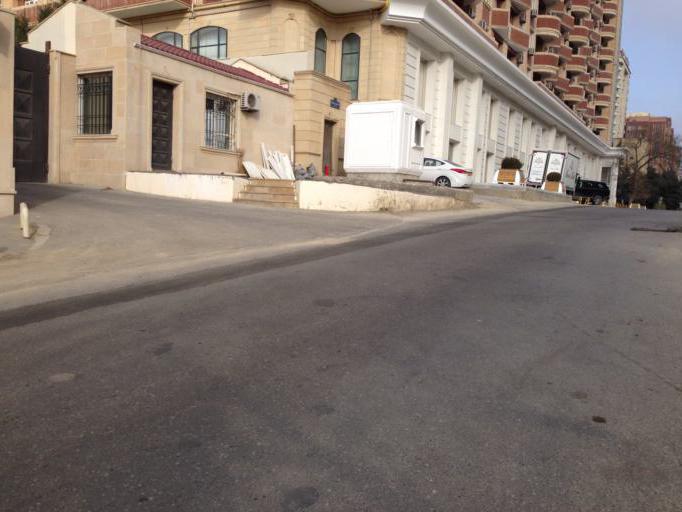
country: AZ
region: Baki
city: Baku
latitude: 40.3963
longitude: 49.8587
